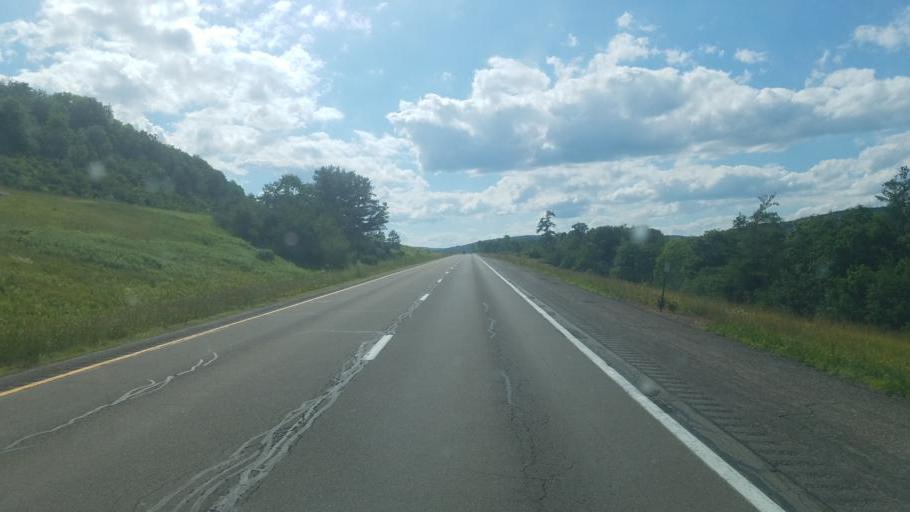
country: US
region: New York
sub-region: Allegany County
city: Alfred
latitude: 42.3157
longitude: -77.7632
